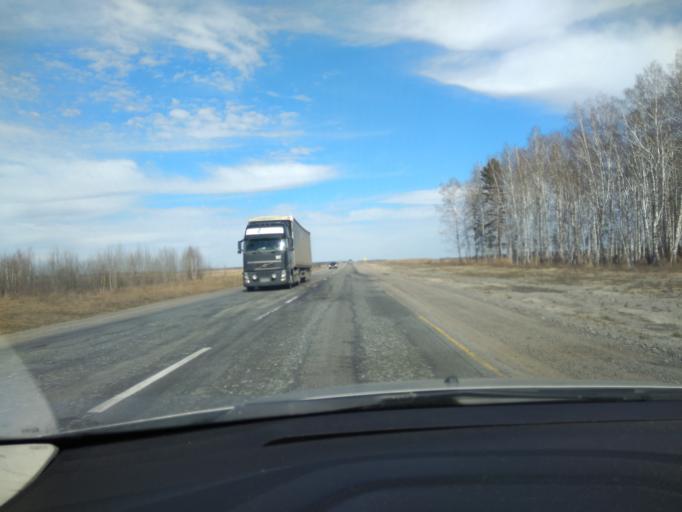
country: RU
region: Sverdlovsk
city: Pyshma
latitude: 56.9120
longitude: 63.1185
